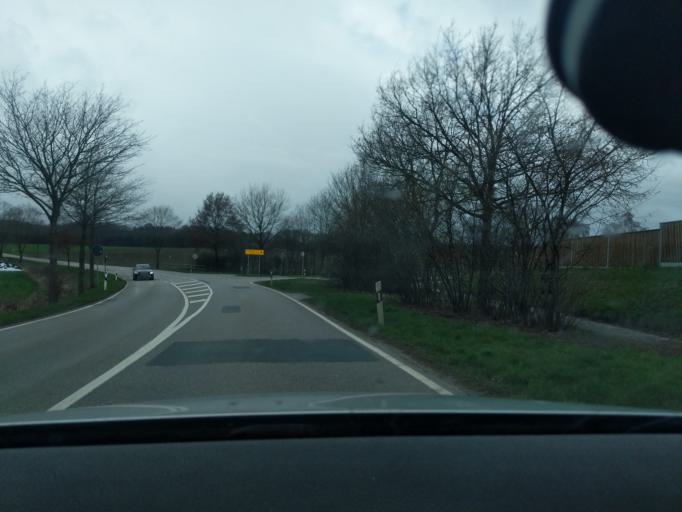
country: DE
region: Lower Saxony
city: Horneburg
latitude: 53.5070
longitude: 9.5608
